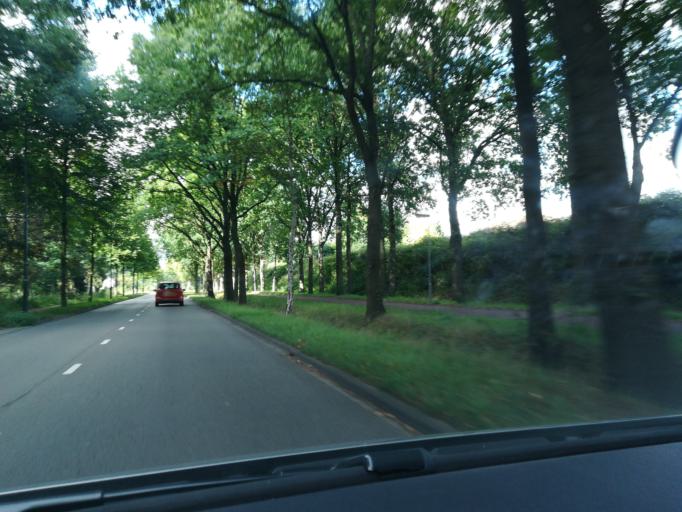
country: NL
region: North Brabant
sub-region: Gemeente Valkenswaard
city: Valkenswaard
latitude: 51.3648
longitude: 5.4460
